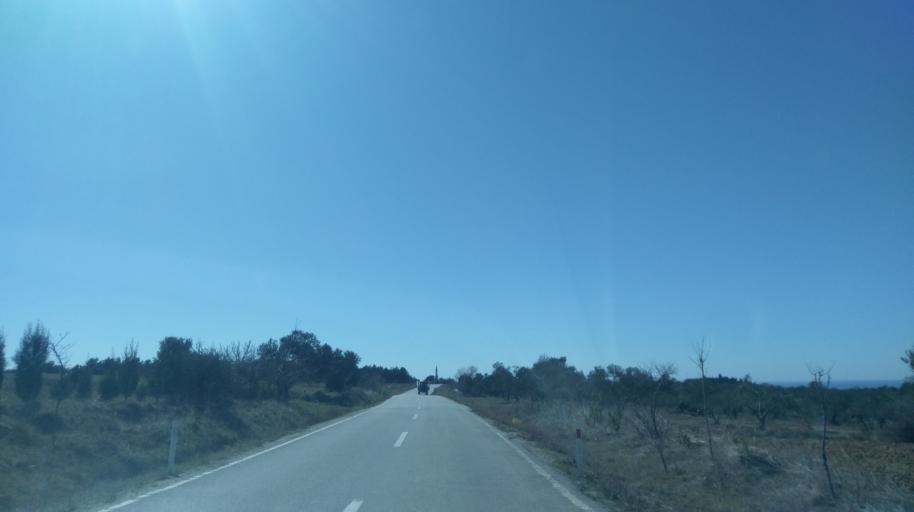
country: TR
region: Canakkale
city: Intepe
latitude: 40.1028
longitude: 26.2308
